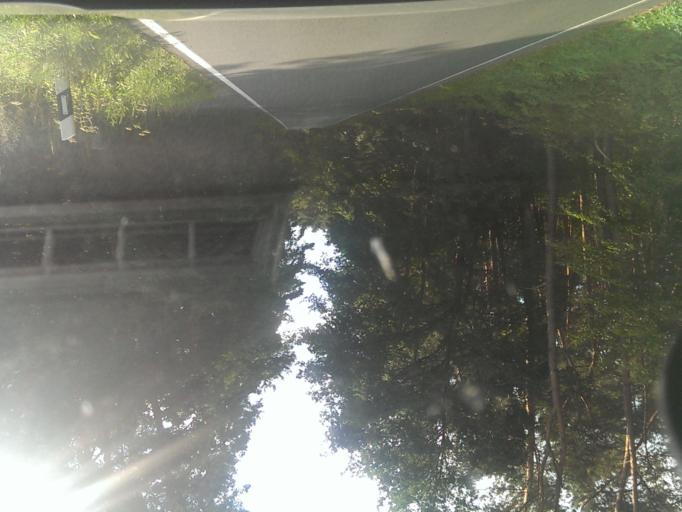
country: DE
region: North Rhine-Westphalia
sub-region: Regierungsbezirk Detmold
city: Delbruck
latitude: 51.7342
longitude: 8.5705
